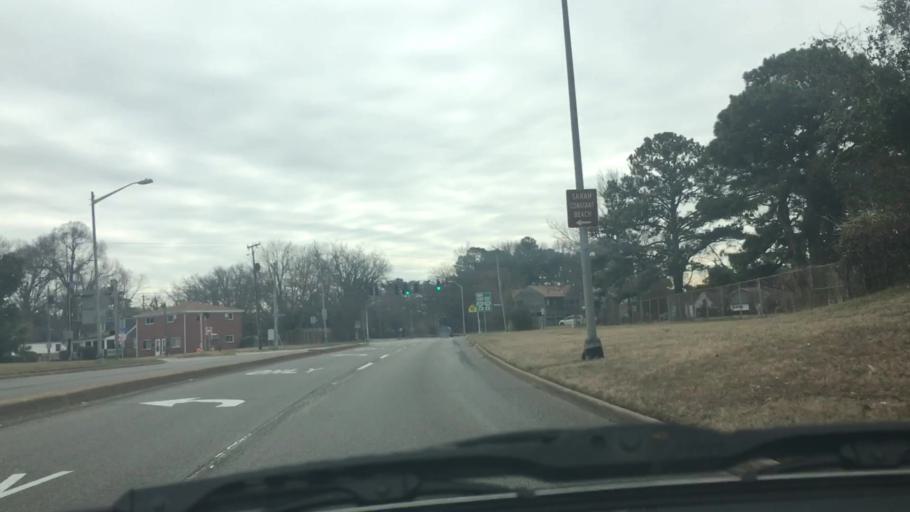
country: US
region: Virginia
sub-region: City of Hampton
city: East Hampton
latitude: 36.9566
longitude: -76.2584
